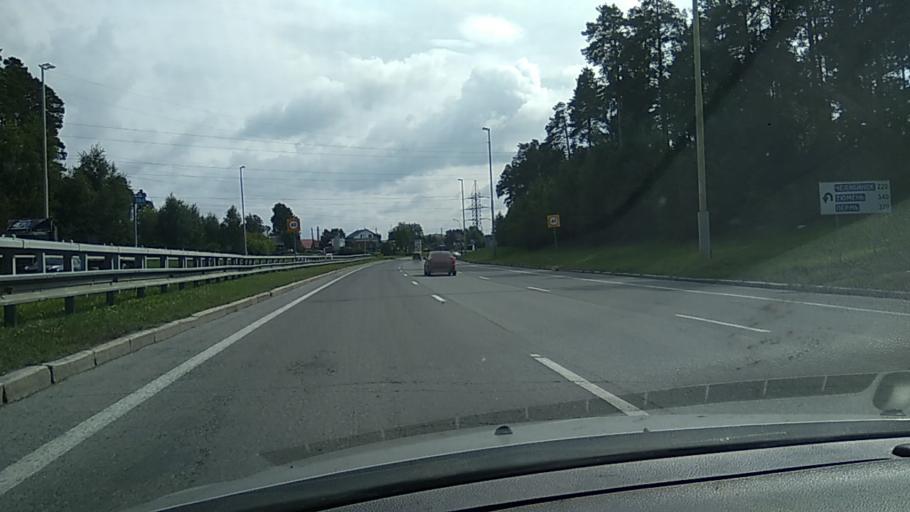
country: RU
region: Sverdlovsk
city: Yekaterinburg
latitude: 56.8865
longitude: 60.5513
